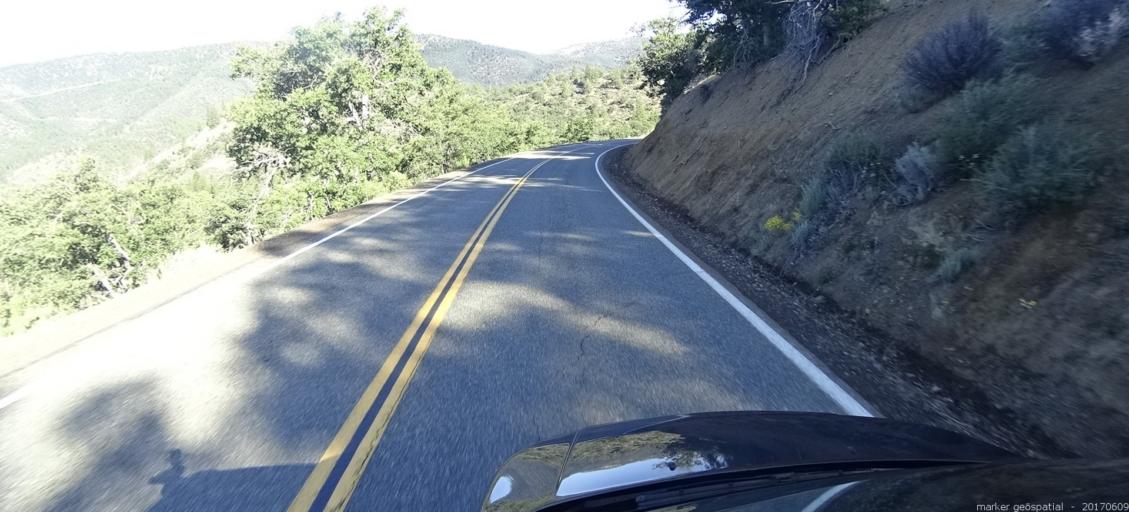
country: US
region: California
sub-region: Siskiyou County
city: Weed
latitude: 41.3520
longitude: -122.7362
